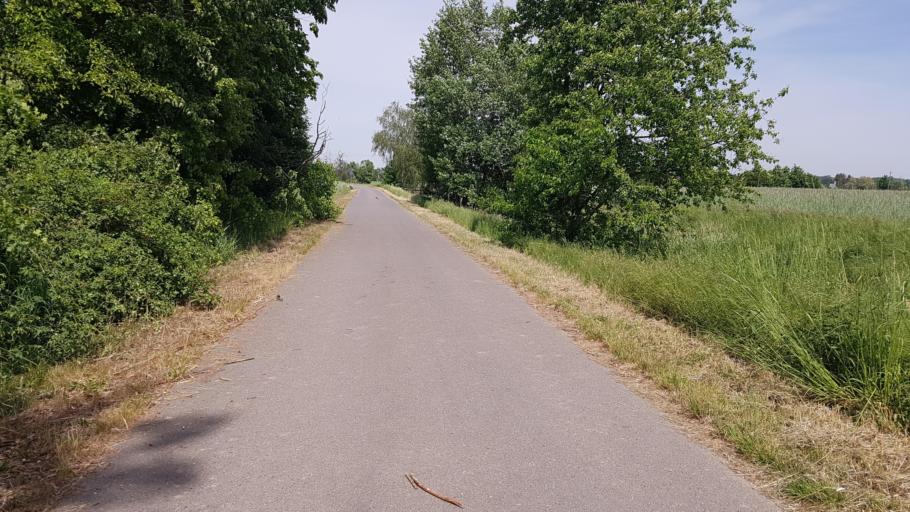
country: DE
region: Brandenburg
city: Grosskmehlen
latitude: 51.3788
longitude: 13.7086
